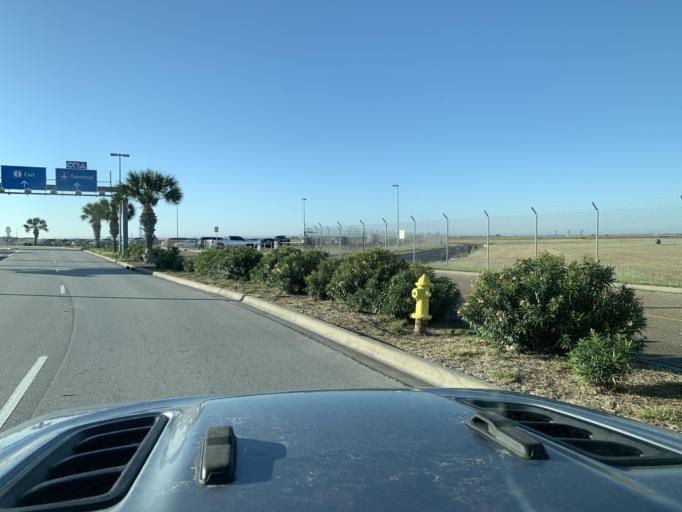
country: US
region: Texas
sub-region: Nueces County
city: Corpus Christi
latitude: 27.7760
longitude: -97.5041
